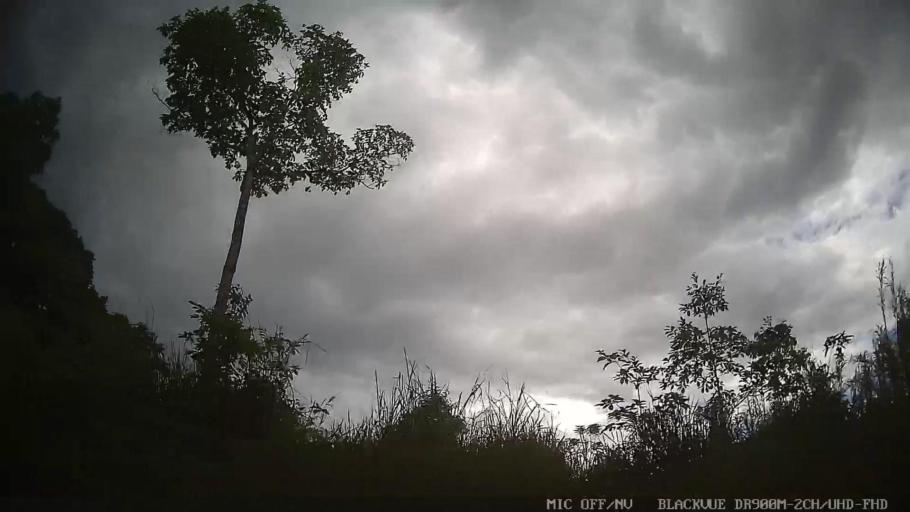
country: BR
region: Sao Paulo
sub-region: Jaguariuna
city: Jaguariuna
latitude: -22.6613
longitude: -46.9722
